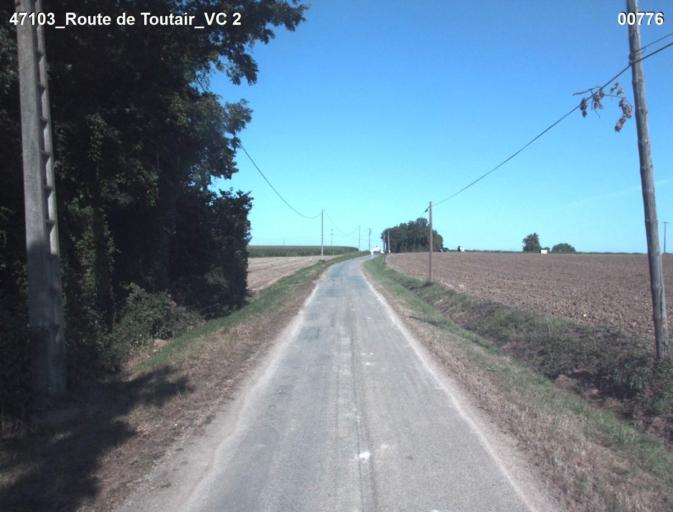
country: FR
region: Aquitaine
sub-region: Departement du Lot-et-Garonne
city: Nerac
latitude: 44.0789
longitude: 0.3236
